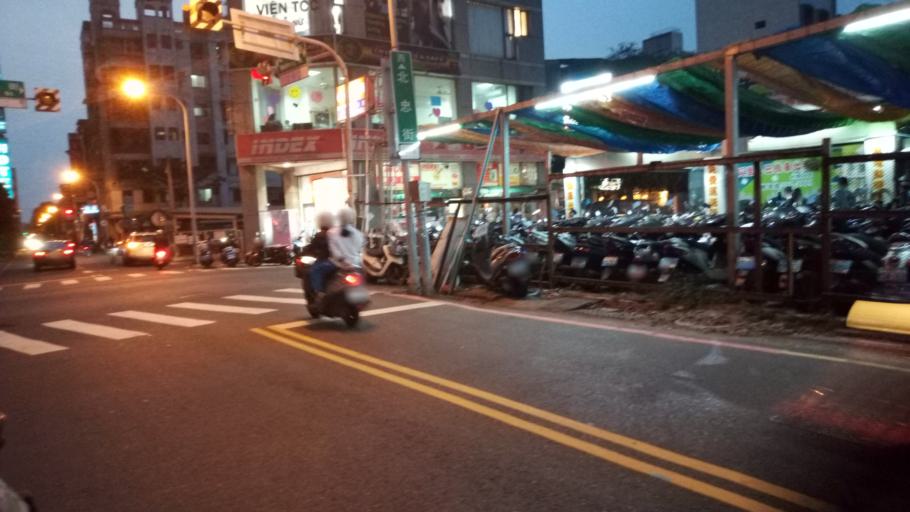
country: TW
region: Taiwan
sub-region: Tainan
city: Tainan
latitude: 22.9987
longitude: 120.2115
